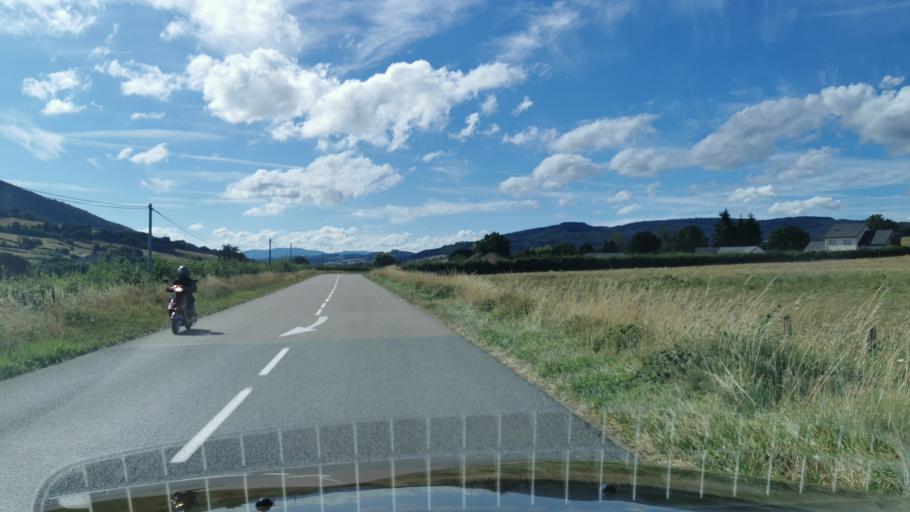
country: FR
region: Bourgogne
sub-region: Departement de Saone-et-Loire
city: Marmagne
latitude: 46.8540
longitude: 4.3202
